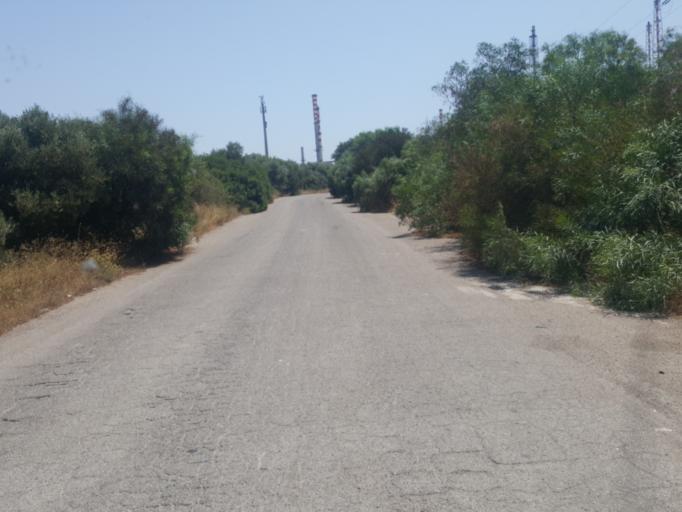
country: IT
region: Apulia
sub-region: Provincia di Taranto
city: Statte
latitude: 40.5017
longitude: 17.1962
